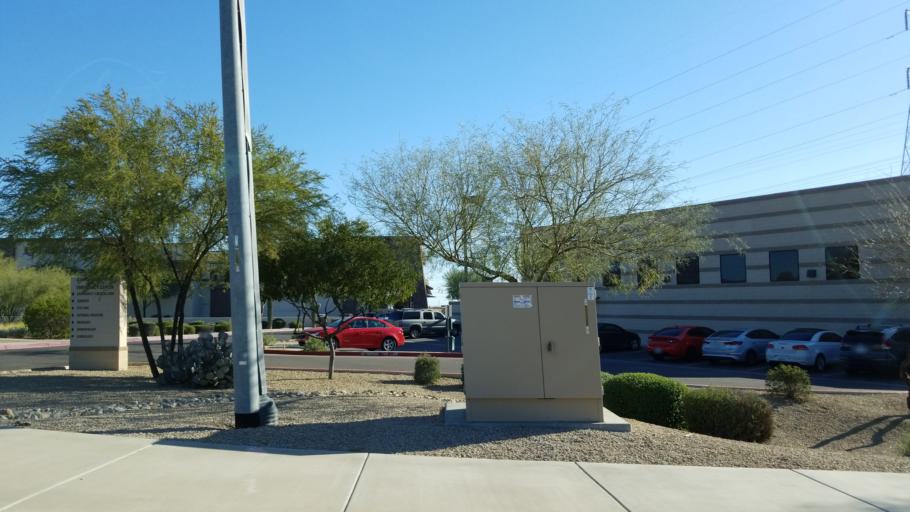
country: US
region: Arizona
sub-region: Maricopa County
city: Carefree
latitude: 33.6914
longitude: -111.9242
